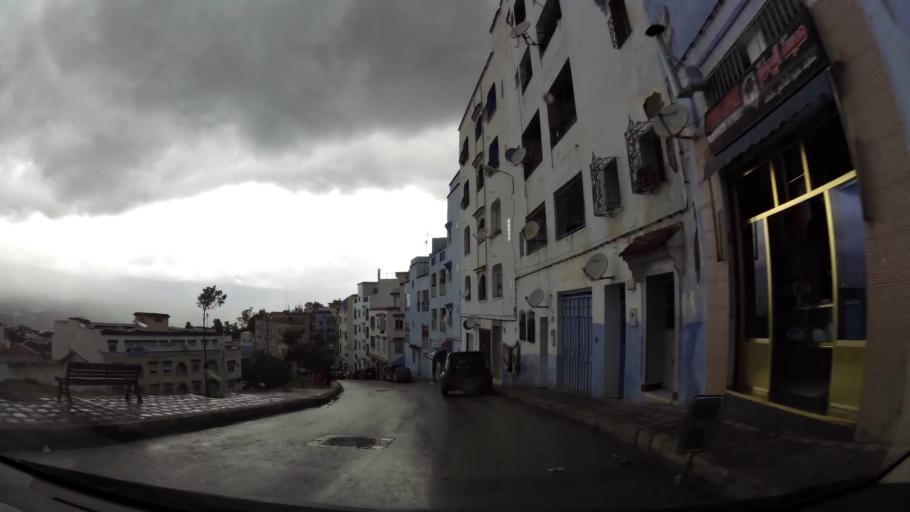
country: MA
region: Tanger-Tetouan
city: Chefchaouene
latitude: 35.1700
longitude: -5.2674
